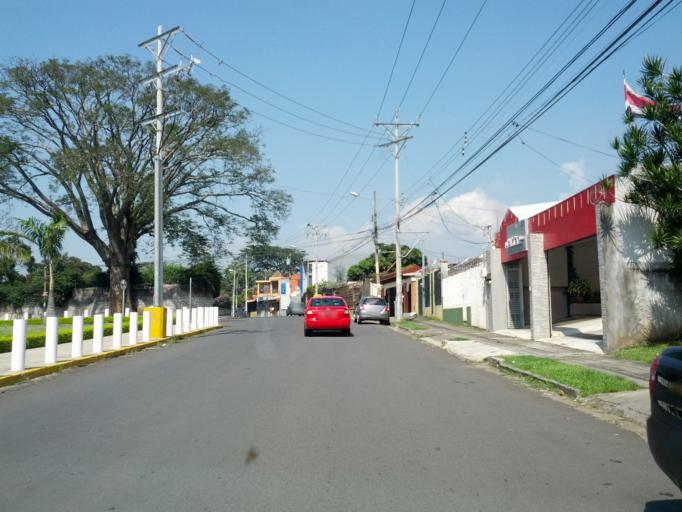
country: CR
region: Alajuela
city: Alajuela
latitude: 10.0132
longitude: -84.2063
